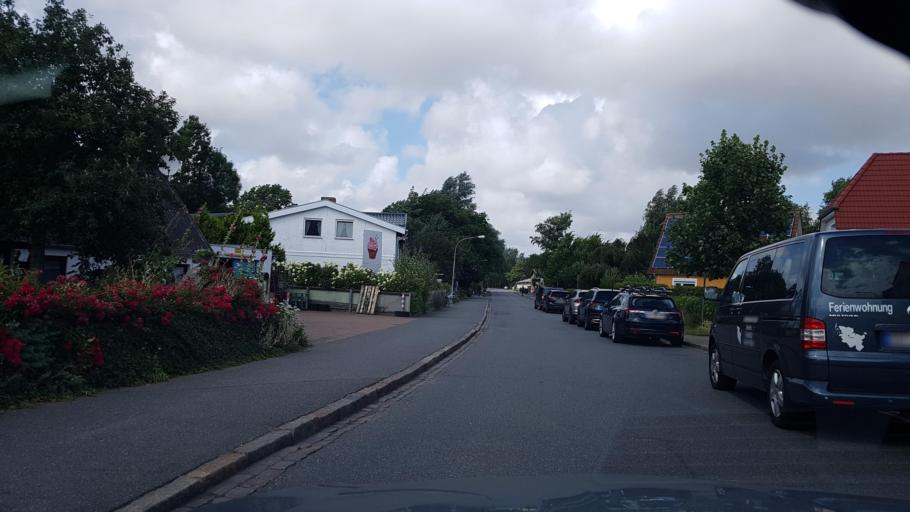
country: DE
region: Schleswig-Holstein
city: Suderdeich
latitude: 54.2017
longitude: 8.9110
